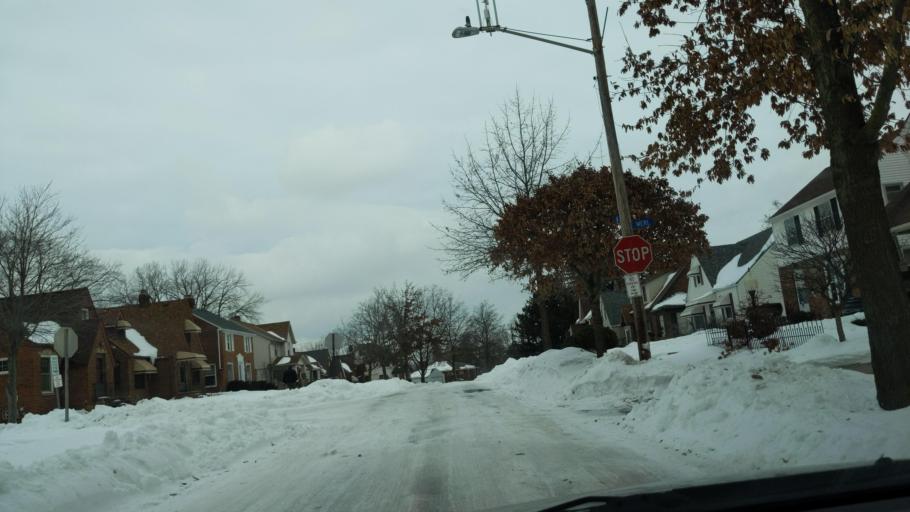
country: US
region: Ohio
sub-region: Cuyahoga County
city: Brooklyn Heights
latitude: 41.4247
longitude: -81.6898
